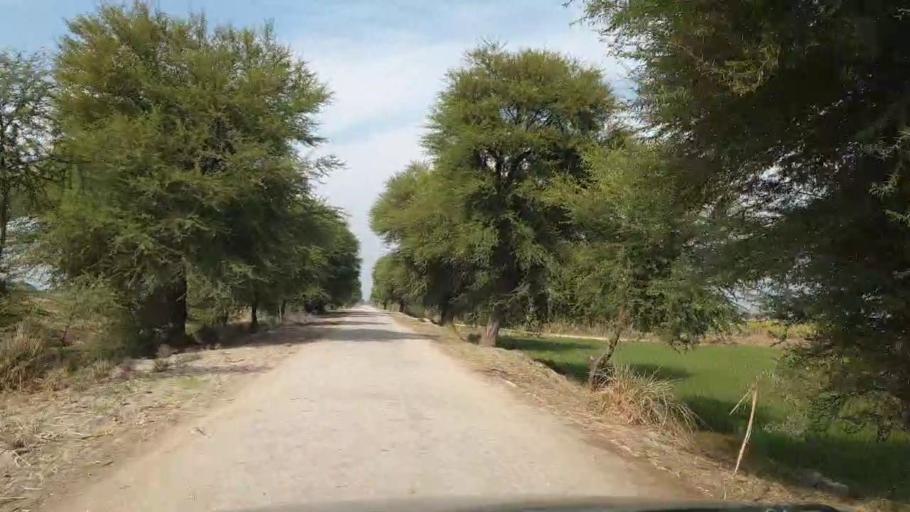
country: PK
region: Sindh
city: Sinjhoro
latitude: 26.1174
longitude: 68.8038
